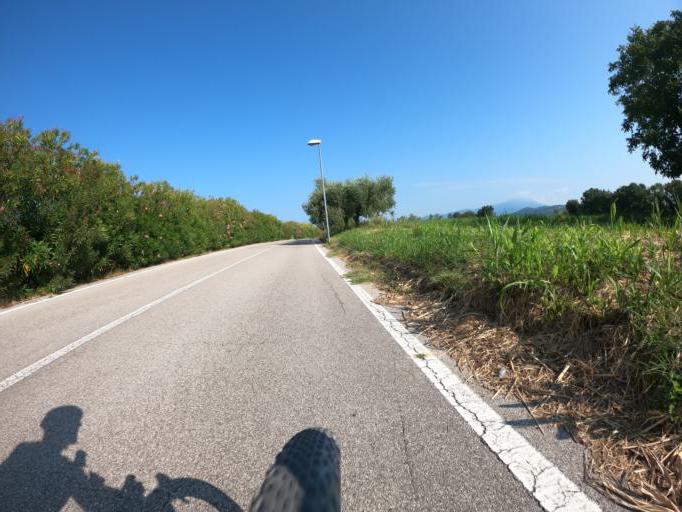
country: IT
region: Veneto
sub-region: Provincia di Verona
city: Lazise
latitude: 45.5146
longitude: 10.7363
